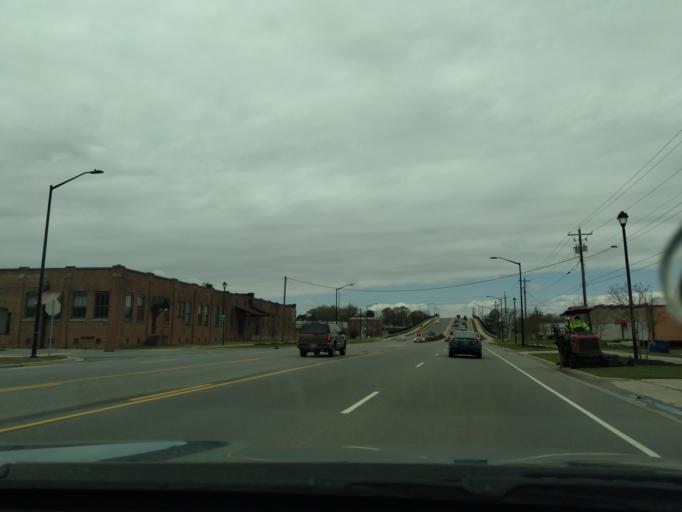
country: US
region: North Carolina
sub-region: Pitt County
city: Greenville
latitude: 35.6063
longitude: -77.3765
